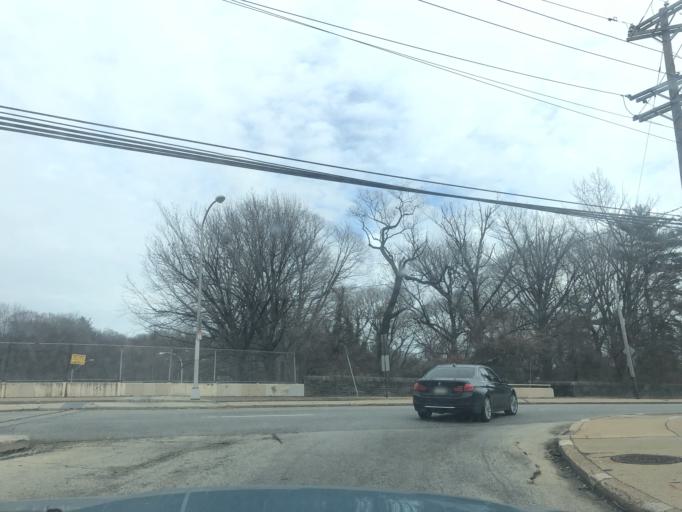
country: US
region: Pennsylvania
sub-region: Montgomery County
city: Bala-Cynwyd
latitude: 40.0174
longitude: -75.1724
